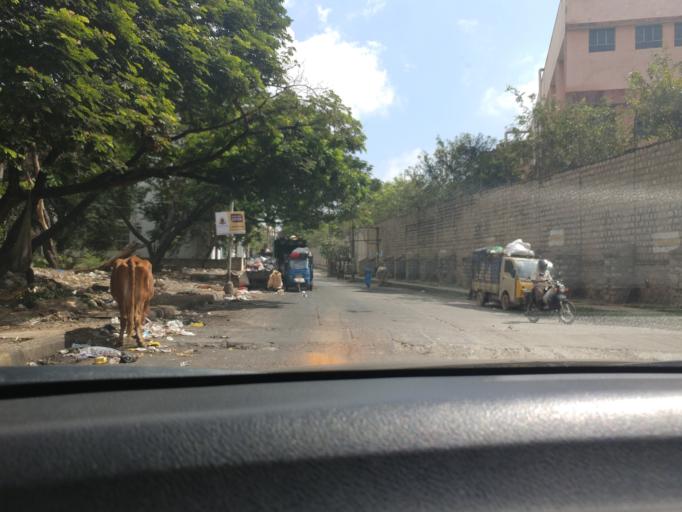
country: IN
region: Karnataka
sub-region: Bangalore Urban
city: Bangalore
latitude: 12.9716
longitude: 77.6629
